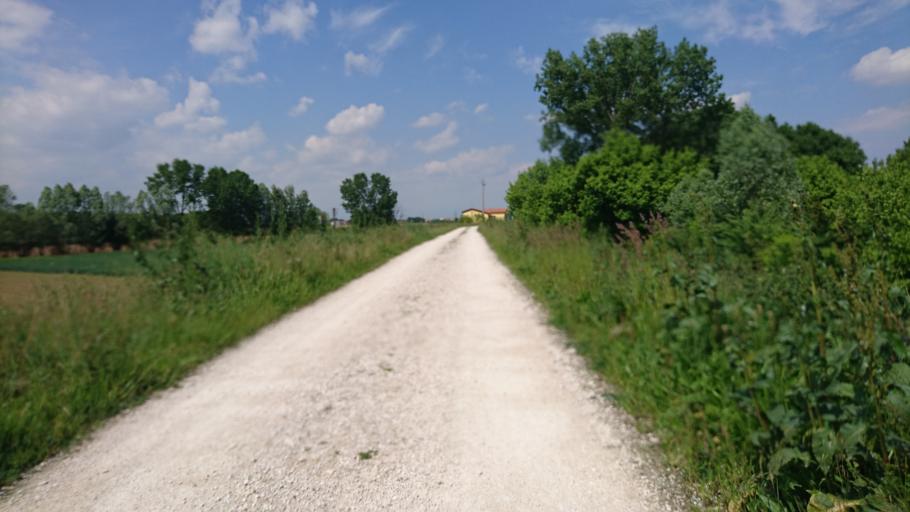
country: IT
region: Veneto
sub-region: Provincia di Padova
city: Veggiano
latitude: 45.4254
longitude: 11.7215
